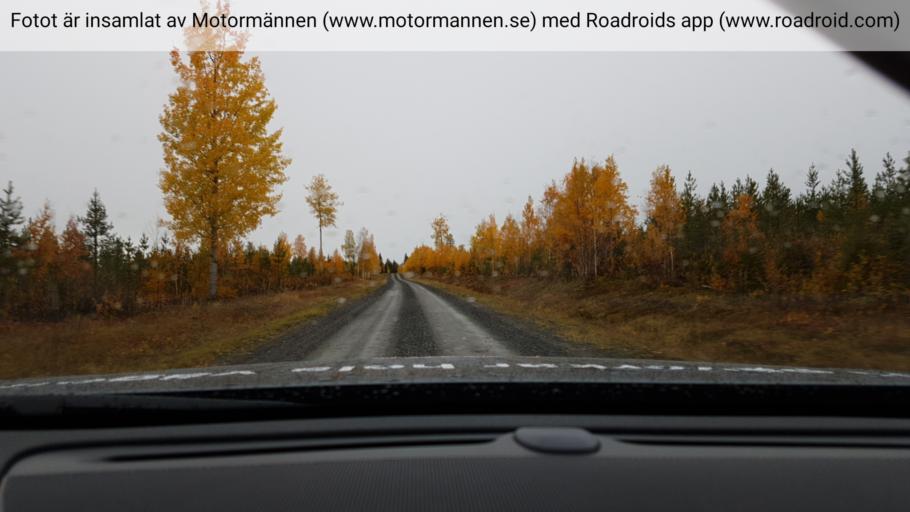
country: SE
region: Norrbotten
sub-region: Pajala Kommun
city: Pajala
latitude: 67.0357
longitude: 22.8468
